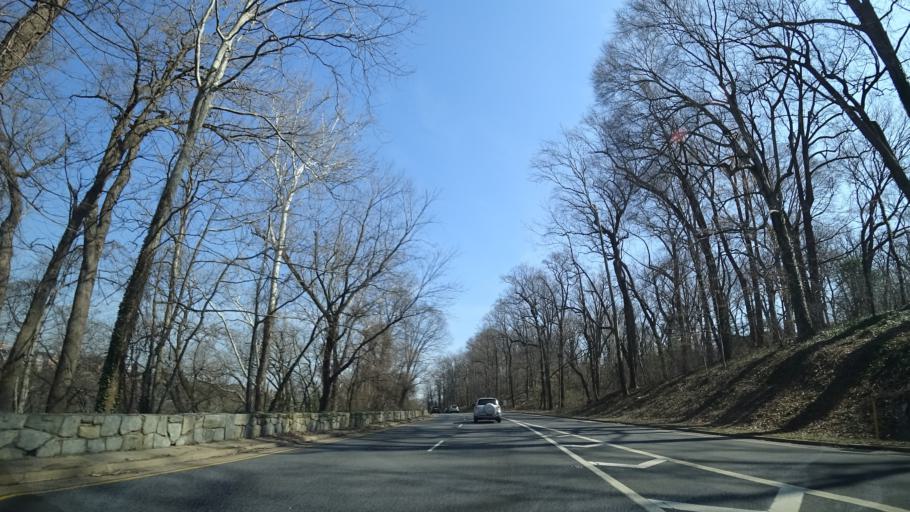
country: US
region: Virginia
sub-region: Arlington County
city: Arlington
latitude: 38.9014
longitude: -77.0820
